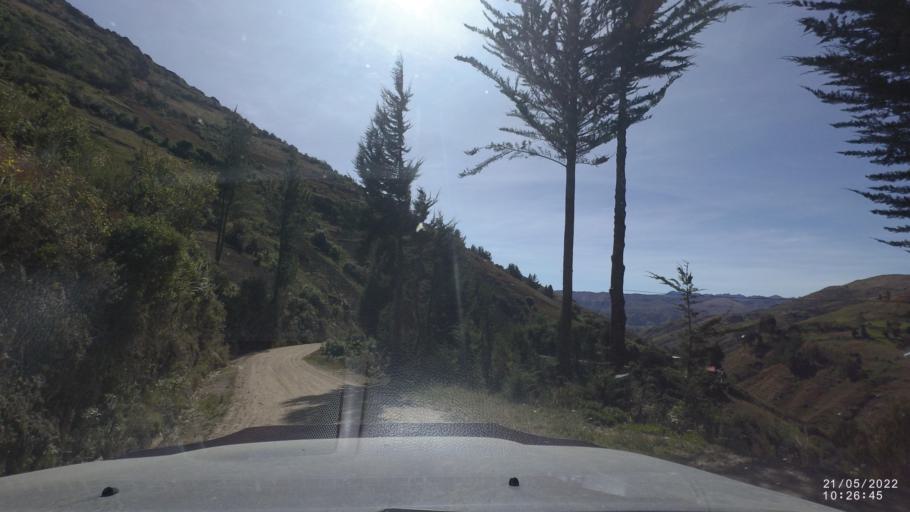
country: BO
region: Cochabamba
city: Colomi
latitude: -17.3238
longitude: -65.9460
